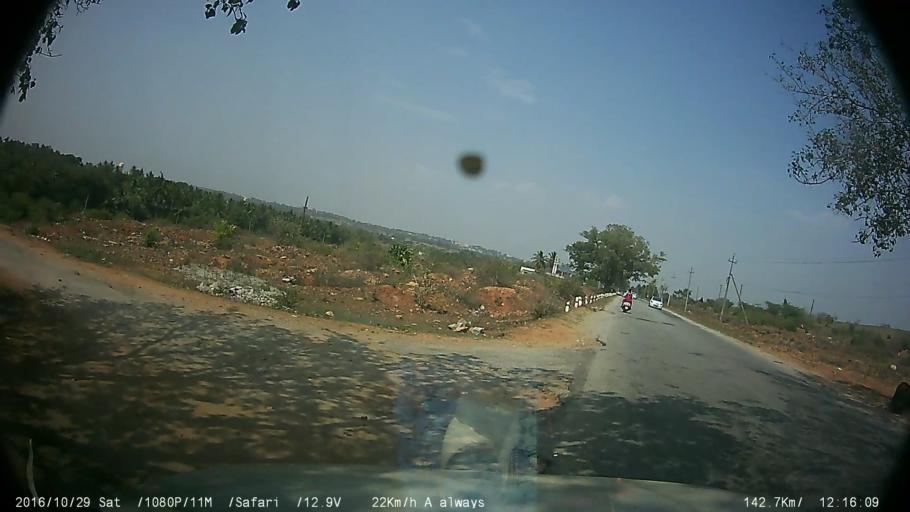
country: IN
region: Karnataka
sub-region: Mysore
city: Mysore
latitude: 12.3781
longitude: 76.5864
